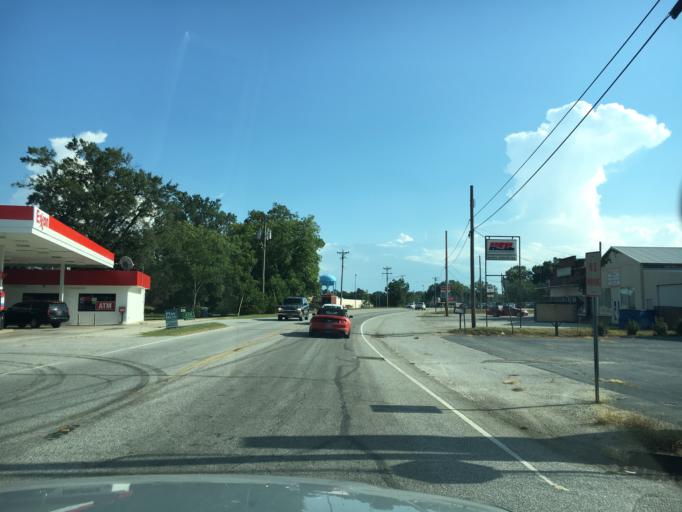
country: US
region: South Carolina
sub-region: Laurens County
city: Clinton
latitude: 34.4591
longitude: -81.8784
